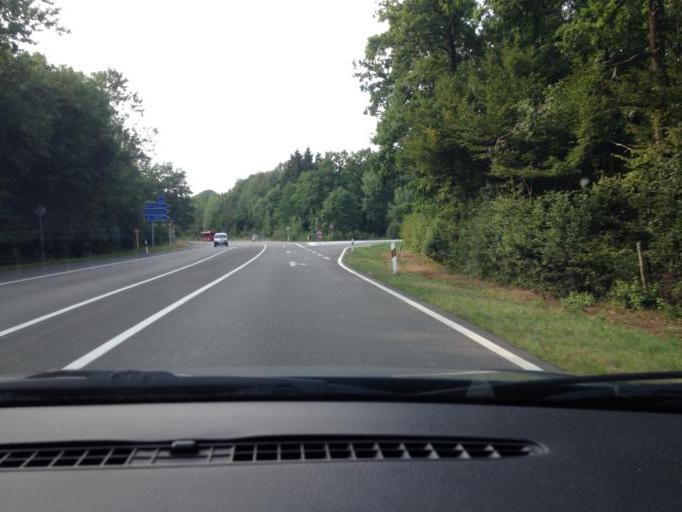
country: DE
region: Rheinland-Pfalz
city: Achtelsbach
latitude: 49.5824
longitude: 7.0880
